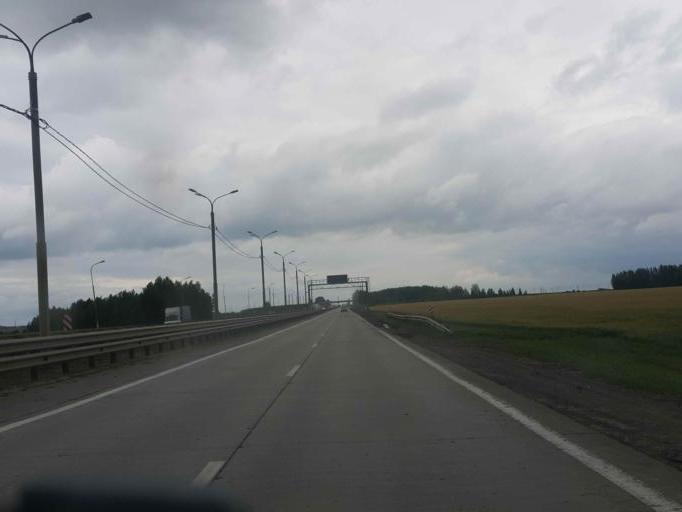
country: RU
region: Tambov
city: Komsomolets
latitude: 52.7393
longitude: 41.2342
